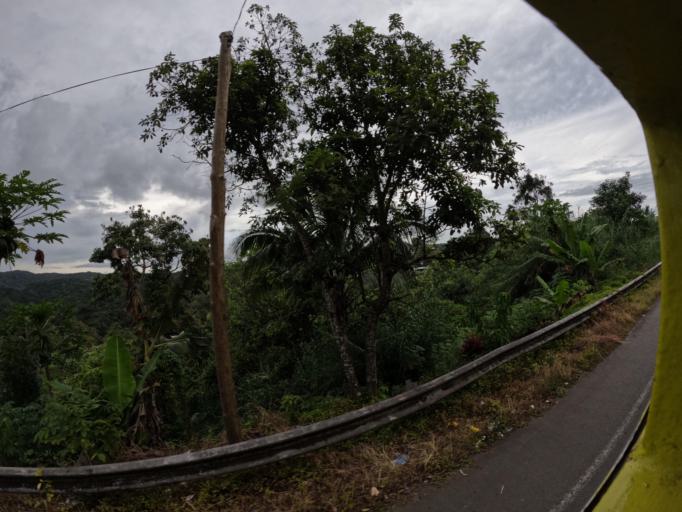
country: FJ
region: Central
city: Suva
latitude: -18.0803
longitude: 178.4577
